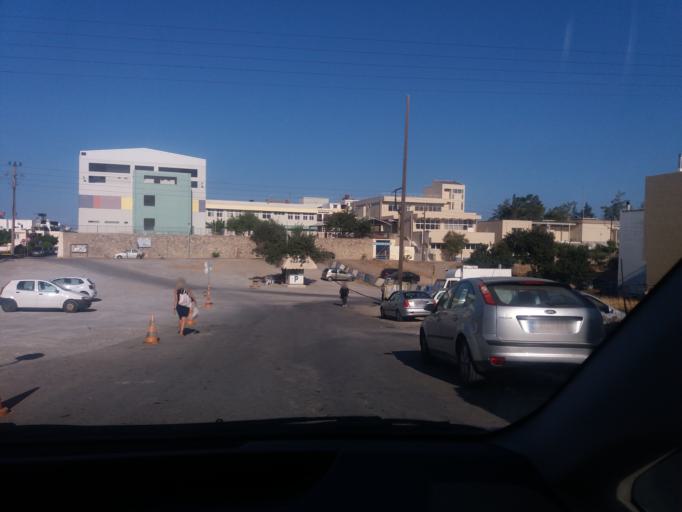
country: GR
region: Crete
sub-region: Nomos Lasithiou
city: Agios Nikolaos
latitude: 35.1936
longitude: 25.7137
